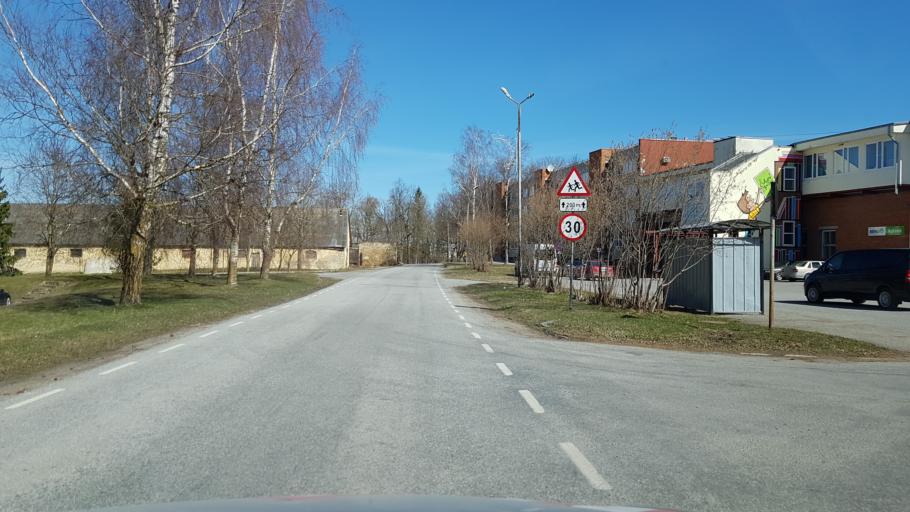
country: EE
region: Laeaene-Virumaa
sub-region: Vinni vald
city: Vinni
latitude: 59.2917
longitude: 26.4275
